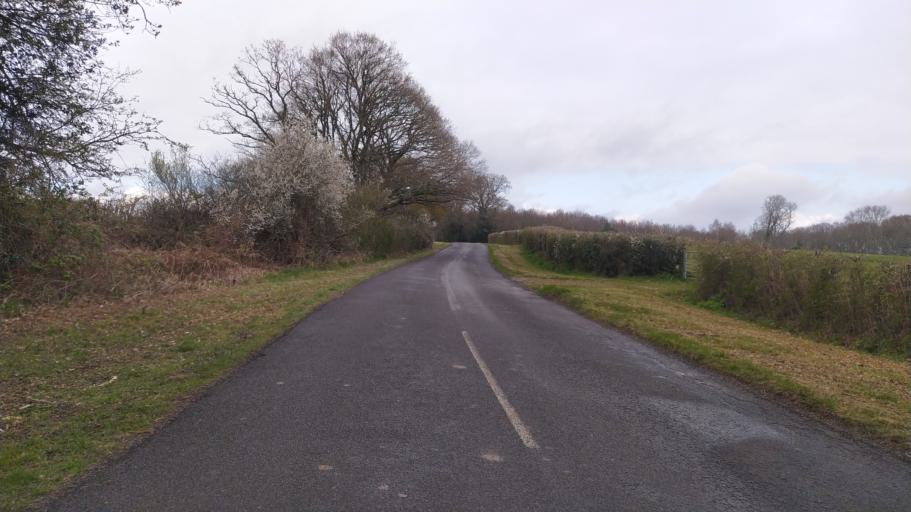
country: GB
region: England
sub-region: West Sussex
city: Petworth
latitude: 51.0090
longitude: -0.6076
